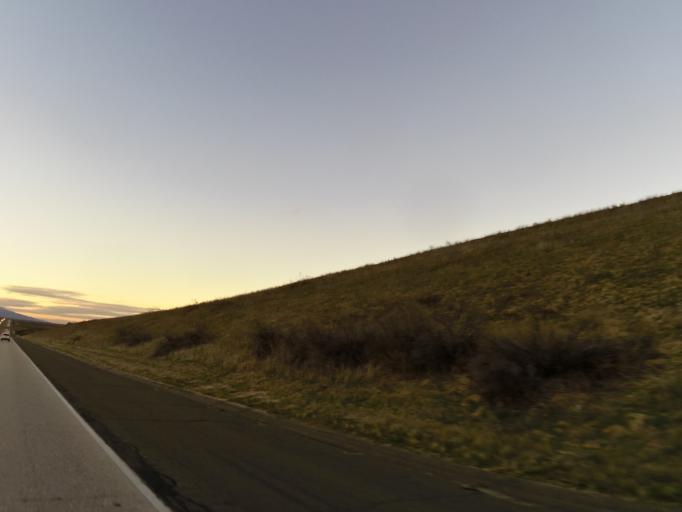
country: US
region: California
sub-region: Monterey County
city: King City
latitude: 36.0740
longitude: -120.9935
